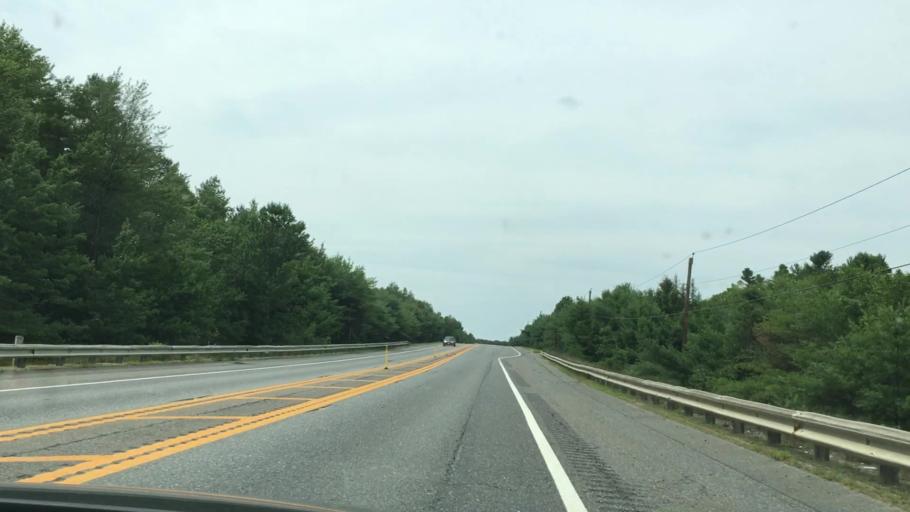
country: US
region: Massachusetts
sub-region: Worcester County
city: Gardner
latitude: 42.6098
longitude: -71.9973
